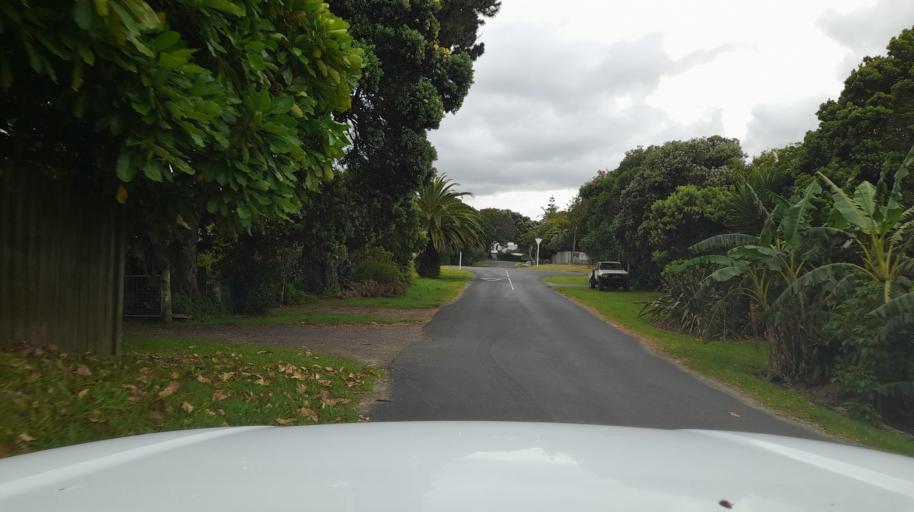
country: NZ
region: Northland
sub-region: Far North District
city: Ahipara
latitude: -35.1618
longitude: 173.1581
